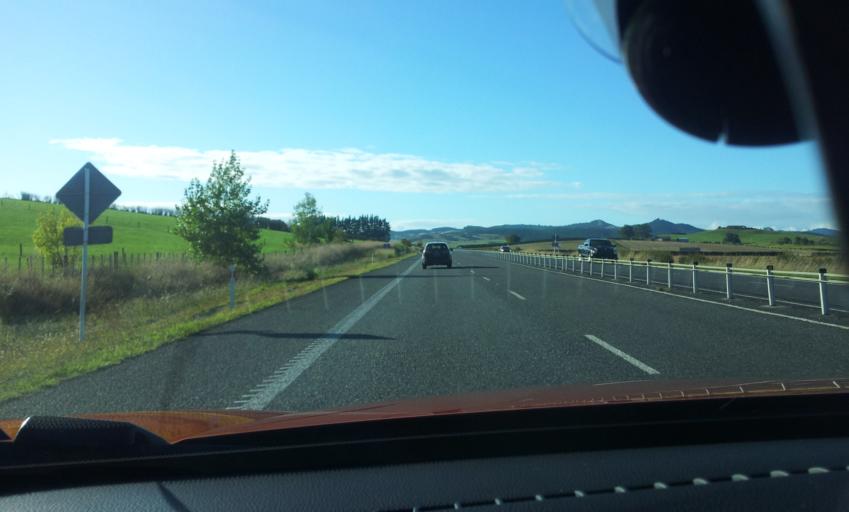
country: NZ
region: Waikato
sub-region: Waikato District
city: Te Kauwhata
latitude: -37.2797
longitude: 175.2972
